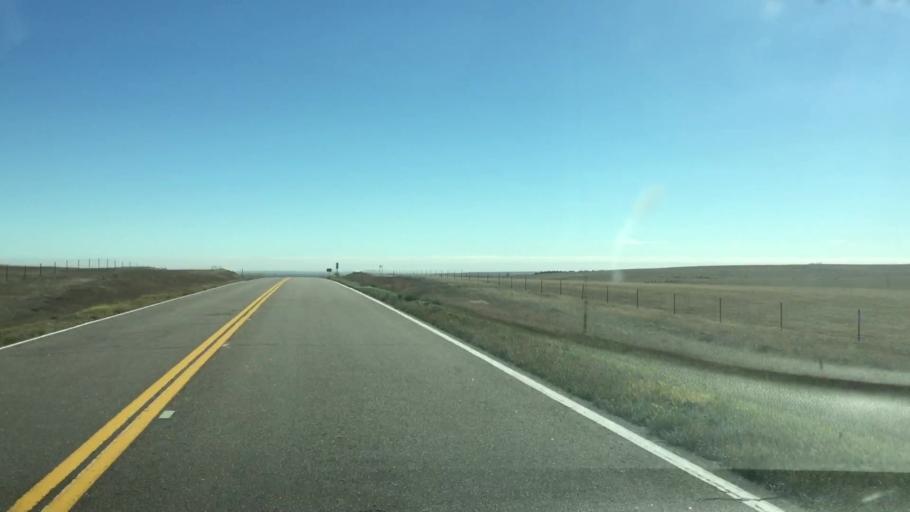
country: US
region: Colorado
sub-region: Lincoln County
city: Limon
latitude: 39.2881
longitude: -103.9710
